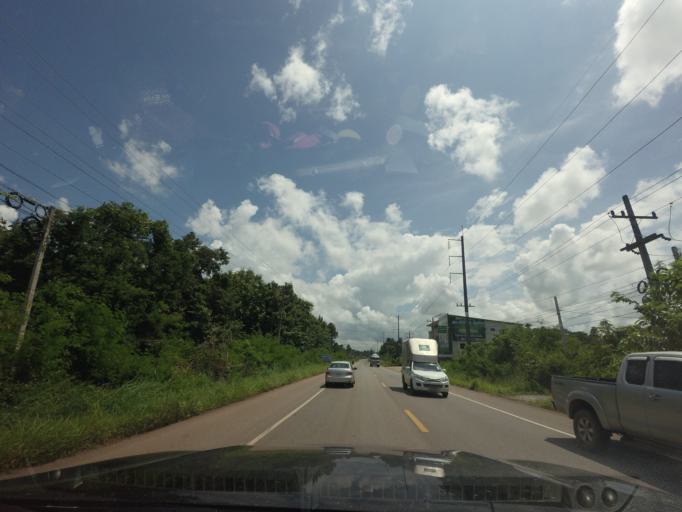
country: TH
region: Changwat Udon Thani
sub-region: Amphoe Ban Phue
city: Ban Phue
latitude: 17.6847
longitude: 102.4967
